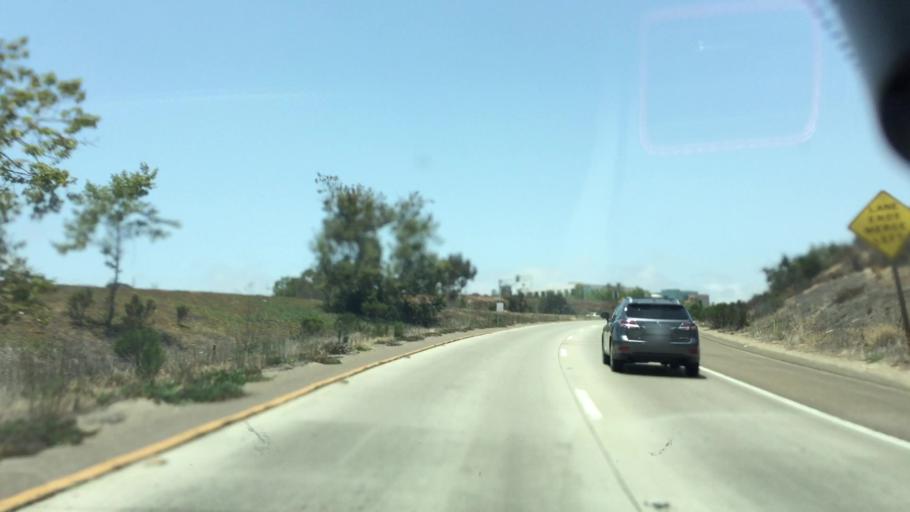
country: US
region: California
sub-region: San Diego County
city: La Jolla
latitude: 32.8485
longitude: -117.1778
